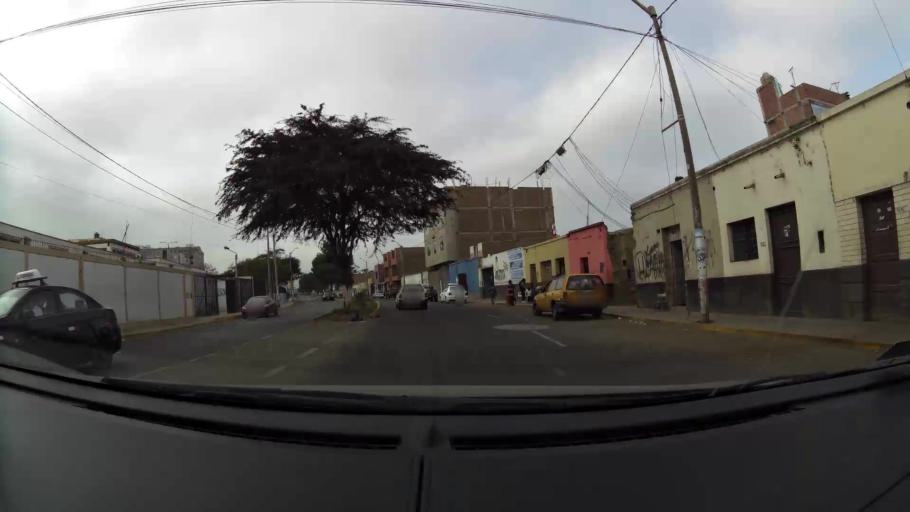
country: PE
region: La Libertad
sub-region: Provincia de Trujillo
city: Trujillo
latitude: -8.1005
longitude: -79.0175
